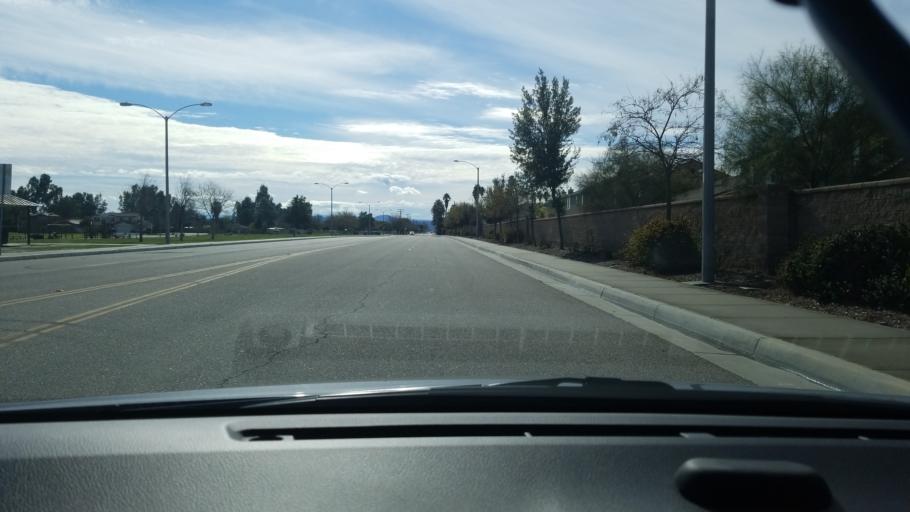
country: US
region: California
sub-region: Riverside County
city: Hemet
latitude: 33.7827
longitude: -117.0155
